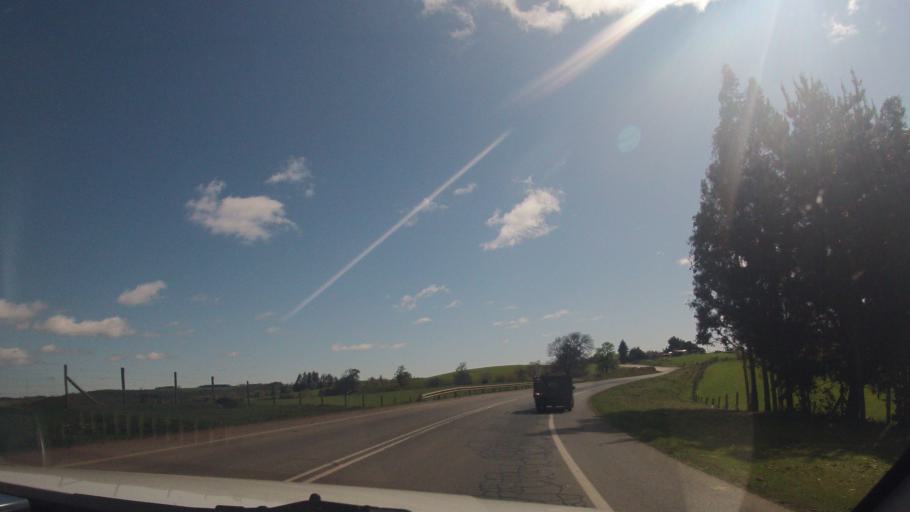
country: CL
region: Araucania
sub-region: Provincia de Malleco
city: Traiguen
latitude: -38.2014
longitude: -72.7631
